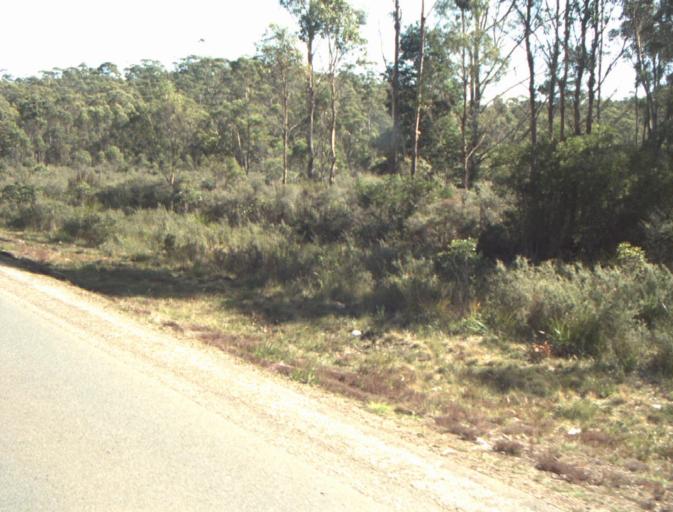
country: AU
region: Tasmania
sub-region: Launceston
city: Mayfield
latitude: -41.3145
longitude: 147.1959
